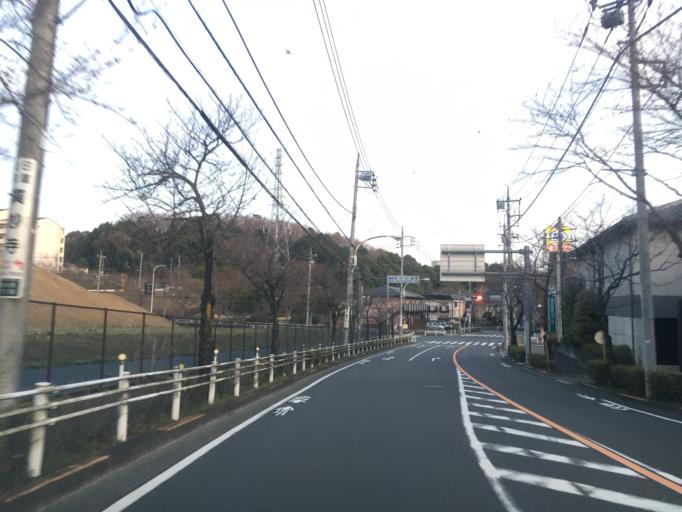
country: JP
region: Tokyo
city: Hino
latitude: 35.6039
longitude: 139.3858
